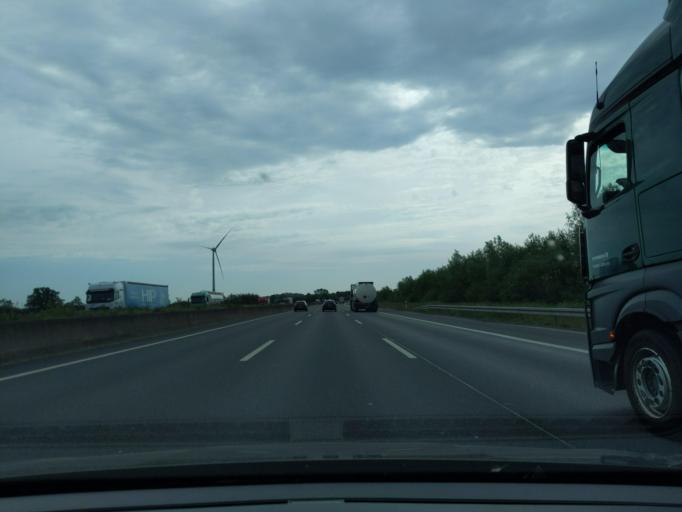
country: DE
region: North Rhine-Westphalia
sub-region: Regierungsbezirk Arnsberg
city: Bonen
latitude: 51.6206
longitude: 7.8085
